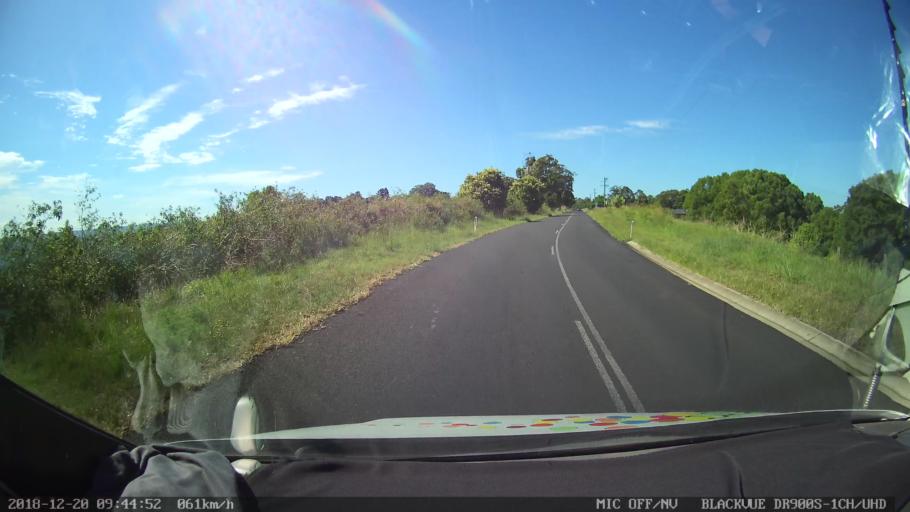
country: AU
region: New South Wales
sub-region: Lismore Municipality
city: Lismore
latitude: -28.7385
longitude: 153.2994
